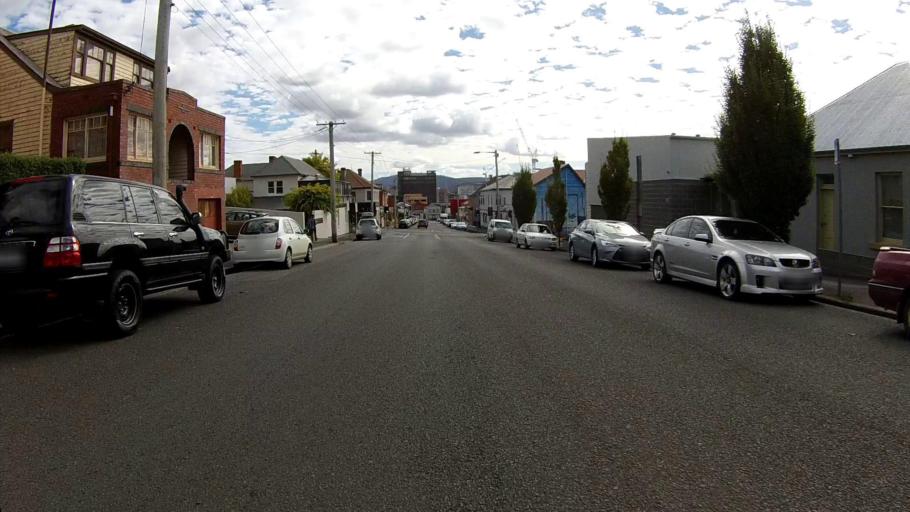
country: AU
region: Tasmania
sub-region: Hobart
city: Sandy Bay
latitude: -42.8854
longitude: 147.3210
